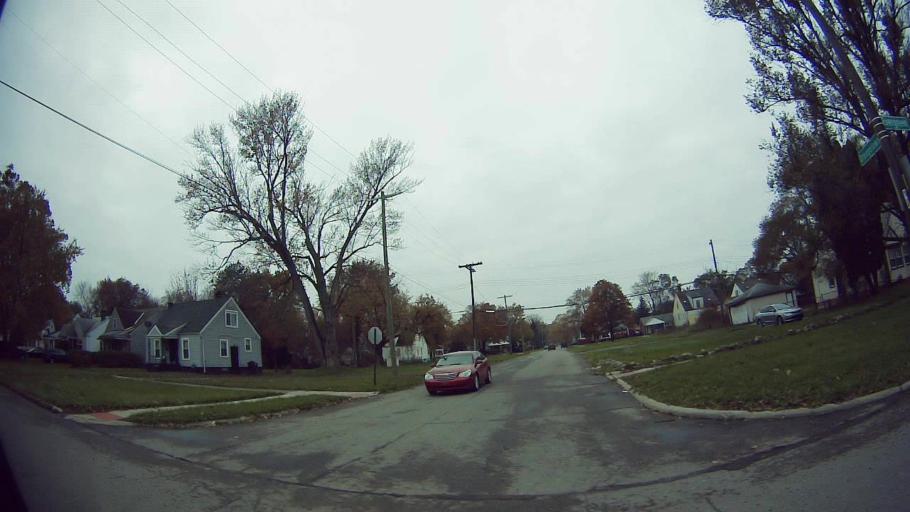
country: US
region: Michigan
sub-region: Wayne County
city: Dearborn Heights
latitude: 42.3671
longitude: -83.2361
